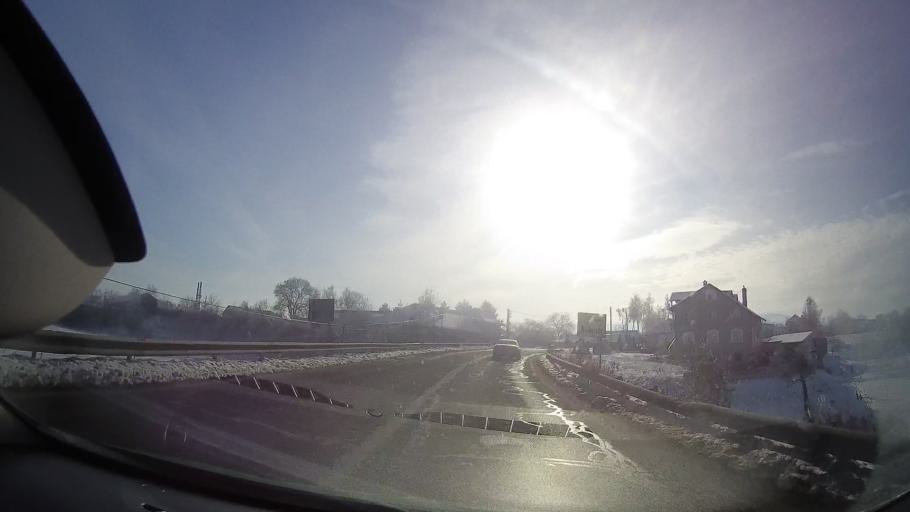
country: RO
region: Neamt
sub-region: Comuna Dobreni
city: Dobreni
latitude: 47.0030
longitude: 26.4236
